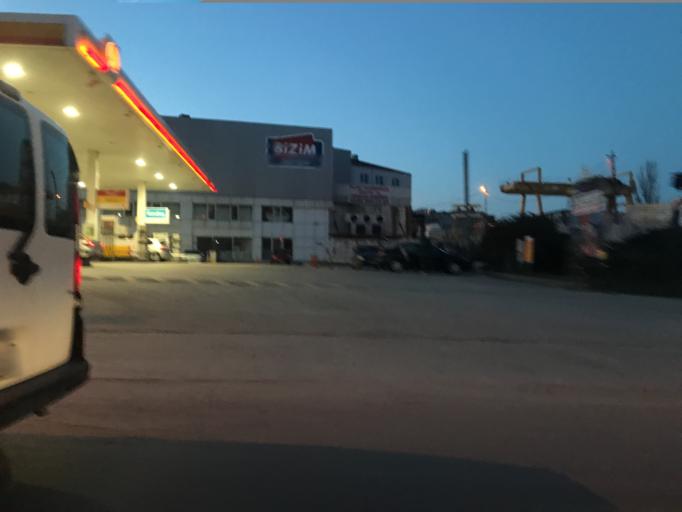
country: TR
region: Istanbul
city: Pendik
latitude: 40.8990
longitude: 29.2691
